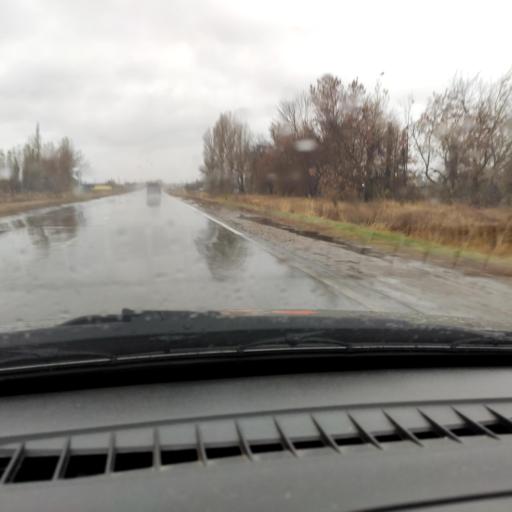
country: RU
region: Samara
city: Tol'yatti
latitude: 53.6341
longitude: 49.3008
